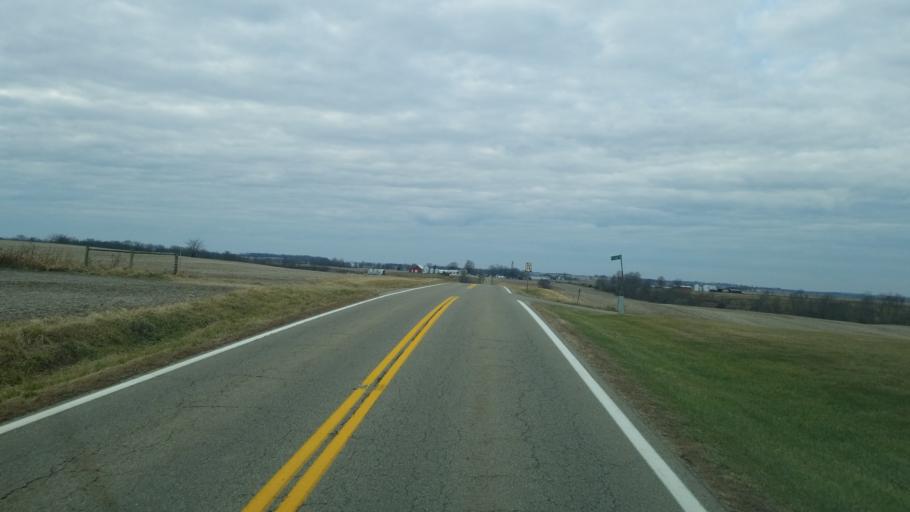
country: US
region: Ohio
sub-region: Highland County
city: Greenfield
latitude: 39.3540
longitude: -83.2893
